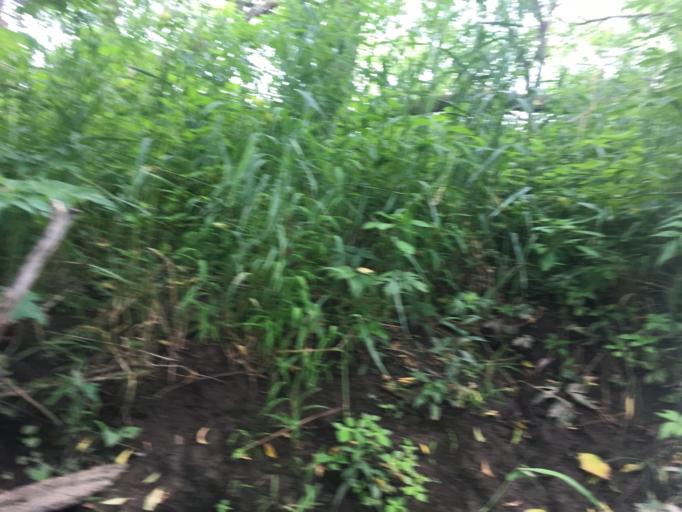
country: US
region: Wisconsin
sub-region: Dunn County
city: Boyceville
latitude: 44.9593
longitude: -92.0603
